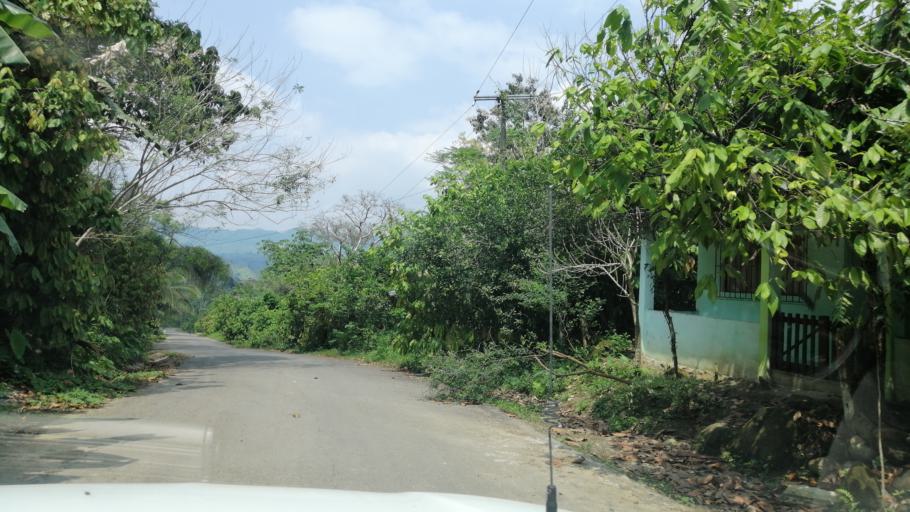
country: MX
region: Chiapas
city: Ostuacan
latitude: 17.3893
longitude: -93.3302
